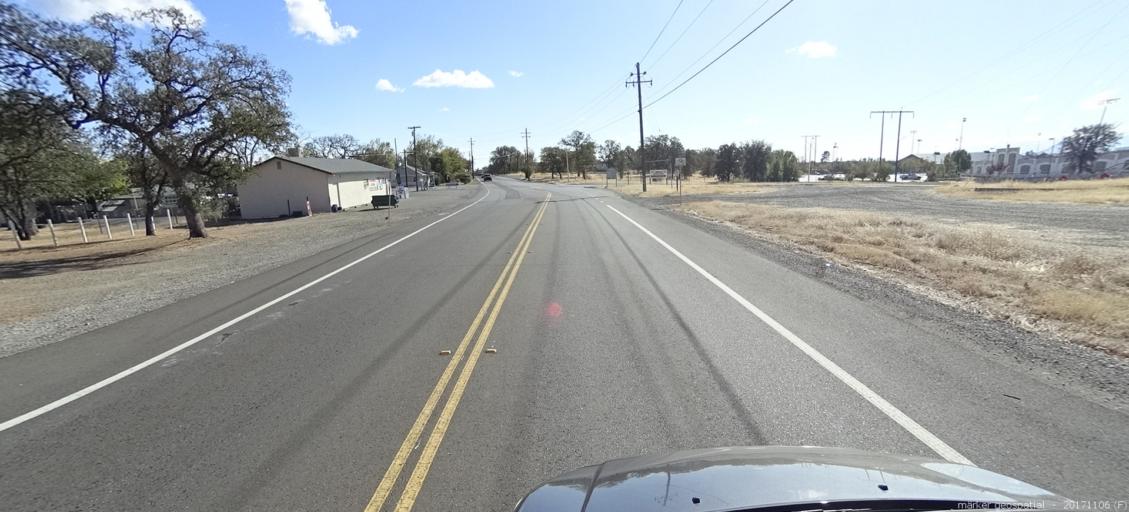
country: US
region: California
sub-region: Shasta County
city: Palo Cedro
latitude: 40.5792
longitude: -122.3059
